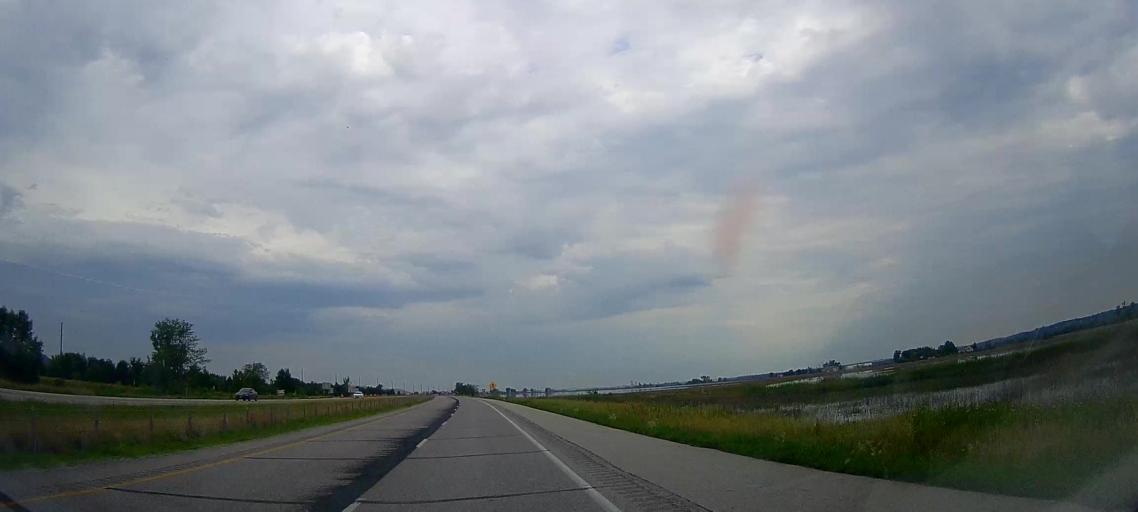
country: US
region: Iowa
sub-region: Pottawattamie County
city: Carter Lake
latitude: 41.4179
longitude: -95.9008
